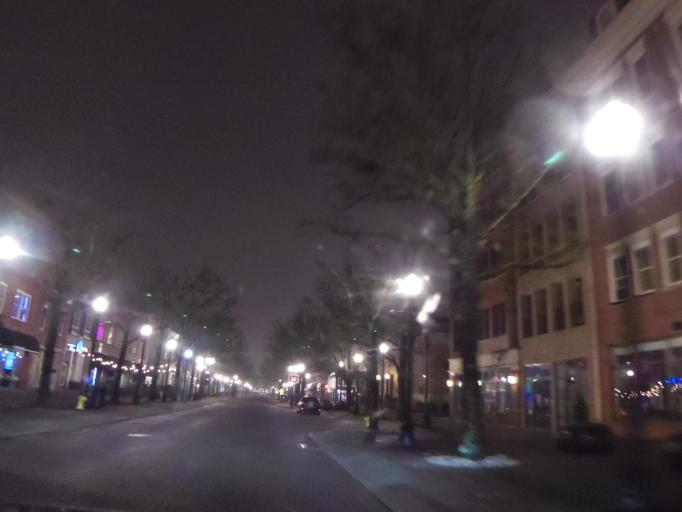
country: US
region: North Carolina
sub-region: Cumberland County
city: Fayetteville
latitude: 35.0538
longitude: -78.8818
